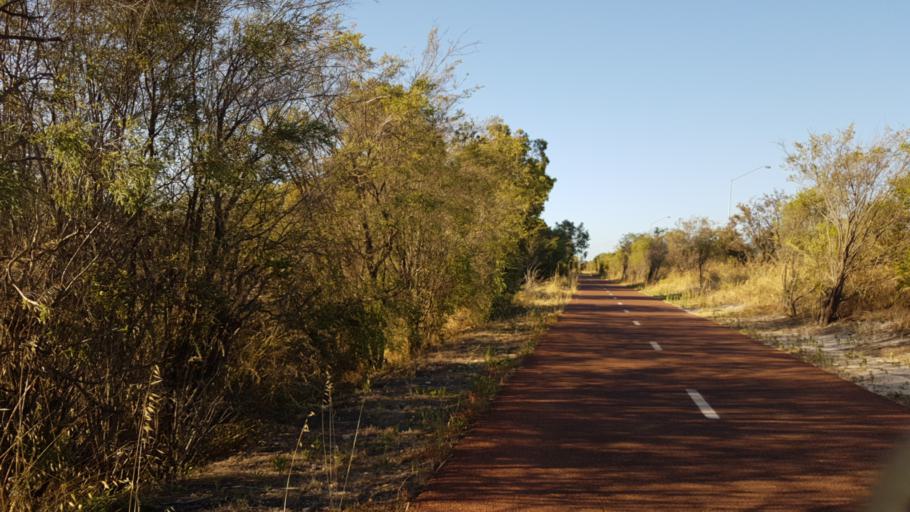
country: AU
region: Western Australia
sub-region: Kwinana
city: Bertram
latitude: -32.2492
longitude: 115.8522
